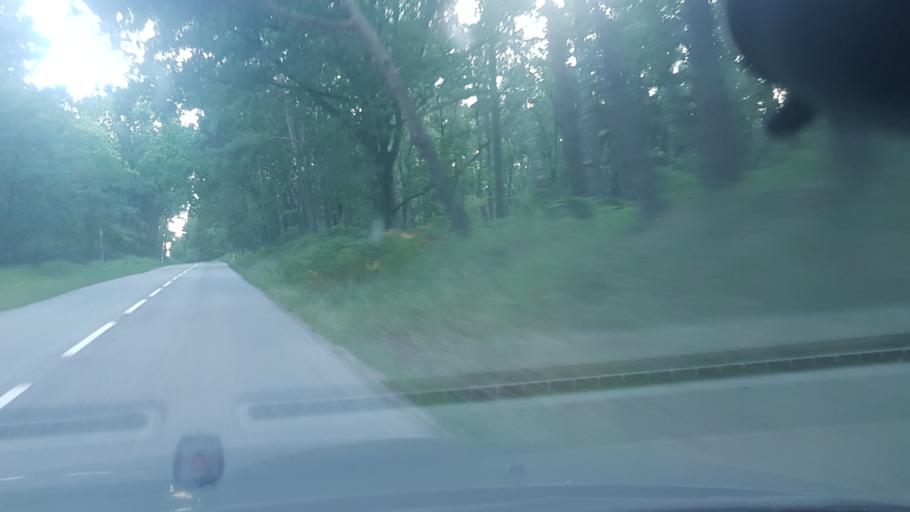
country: PL
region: Pomeranian Voivodeship
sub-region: Powiat nowodworski
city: Sztutowo
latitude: 54.3540
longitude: 19.3085
